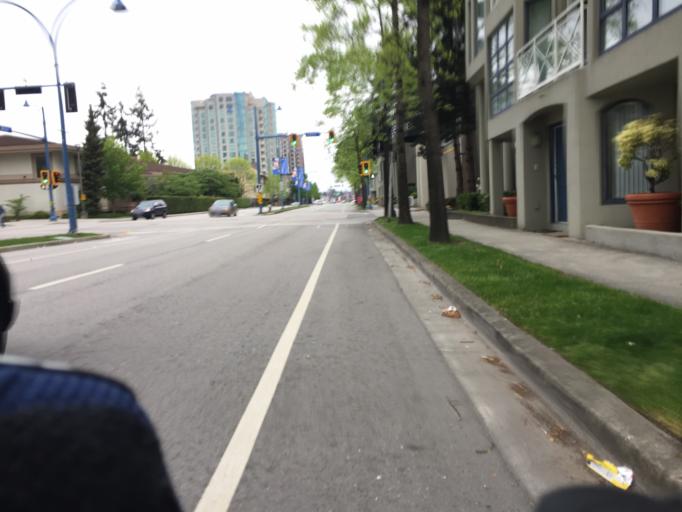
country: CA
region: British Columbia
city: Richmond
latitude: 49.1682
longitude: -123.1402
